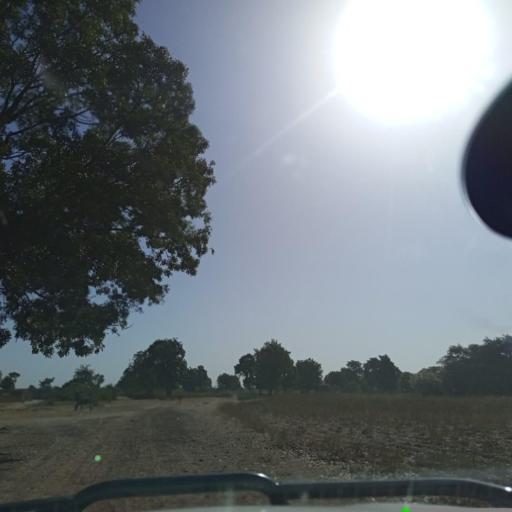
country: ML
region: Koulikoro
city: Koulikoro
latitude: 12.6926
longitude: -7.3745
